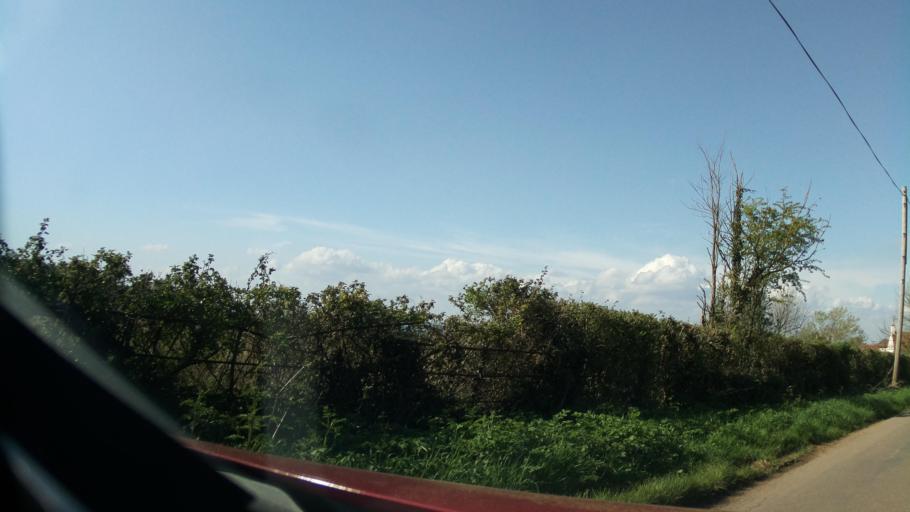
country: GB
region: England
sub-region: South Gloucestershire
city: Alveston
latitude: 51.6058
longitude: -2.5476
